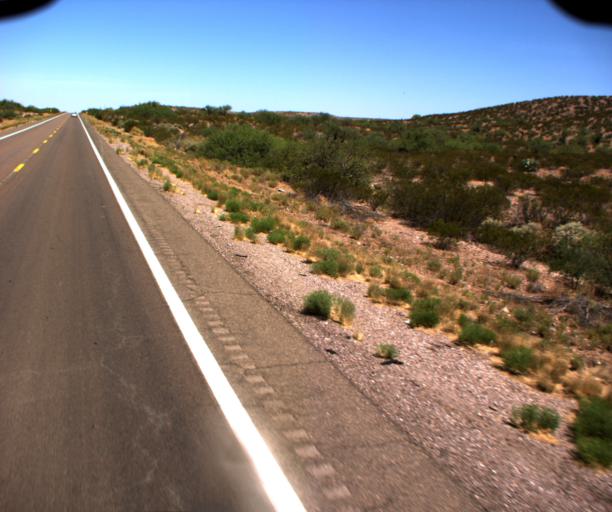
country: US
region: Arizona
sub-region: Graham County
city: Bylas
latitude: 33.1929
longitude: -110.1743
